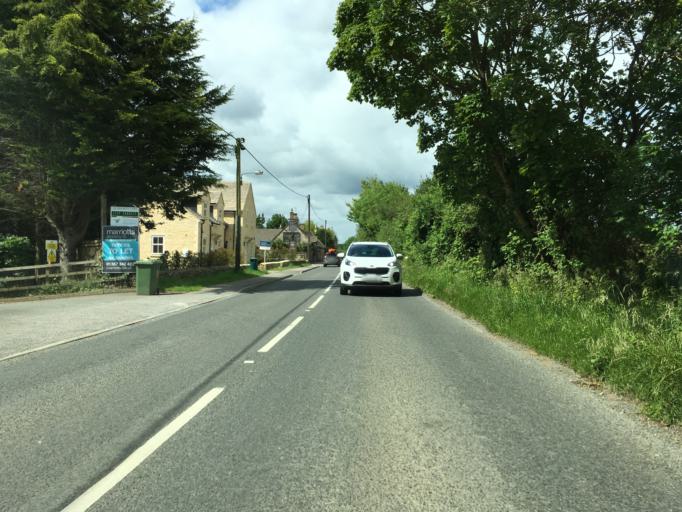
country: GB
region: England
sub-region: Oxfordshire
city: Burford
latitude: 51.8139
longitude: -1.6301
